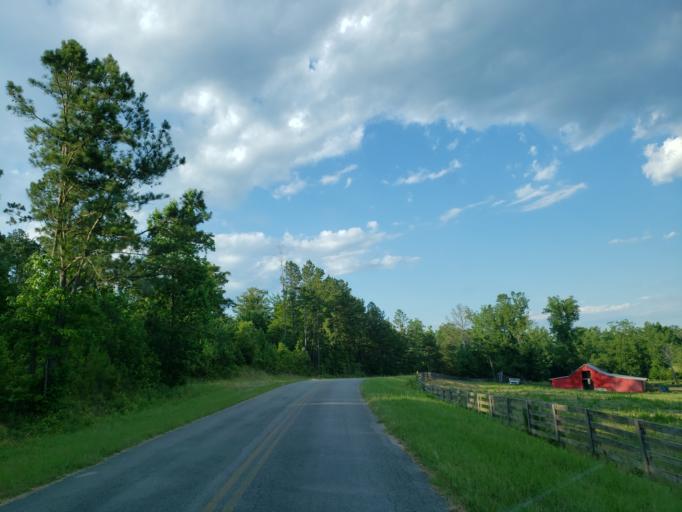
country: US
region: Georgia
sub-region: Haralson County
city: Tallapoosa
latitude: 33.8237
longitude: -85.2825
